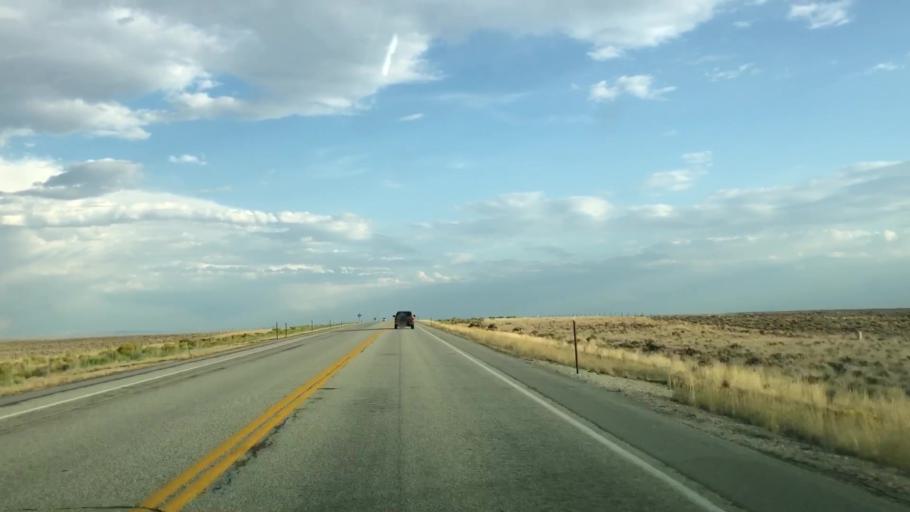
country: US
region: Wyoming
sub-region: Sublette County
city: Marbleton
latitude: 42.3214
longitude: -109.5093
